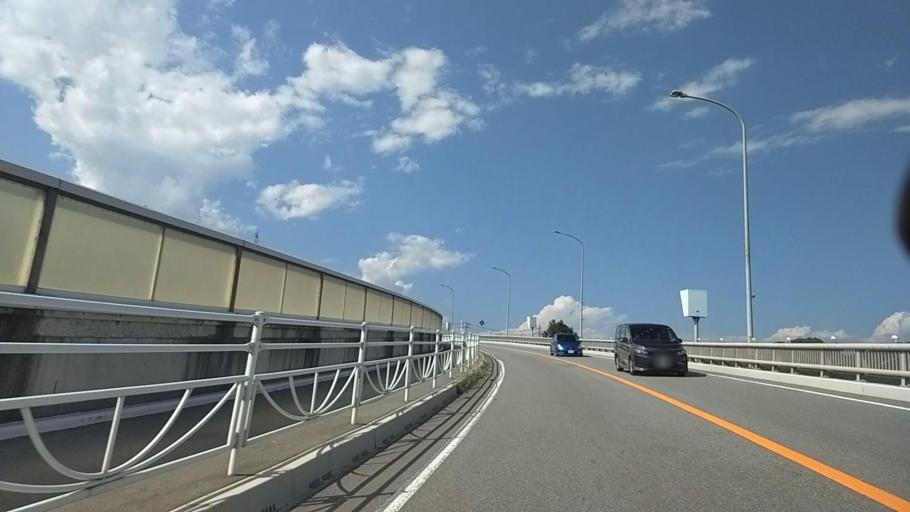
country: JP
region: Shizuoka
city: Fujinomiya
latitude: 35.3812
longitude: 138.4491
